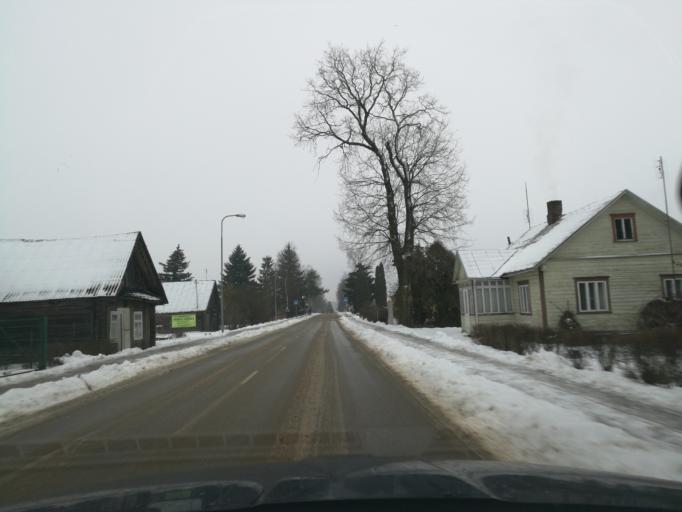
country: LT
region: Utenos apskritis
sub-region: Anyksciai
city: Anyksciai
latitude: 55.4118
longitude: 25.0638
